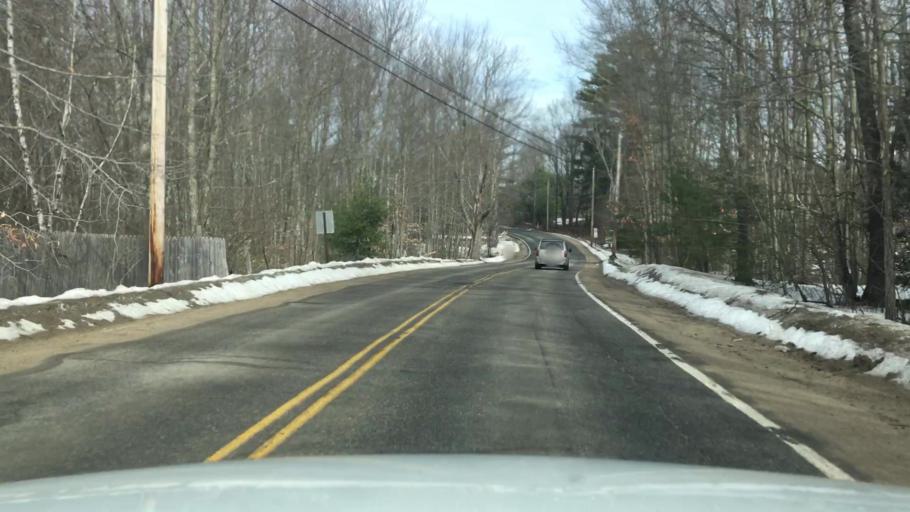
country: US
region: Maine
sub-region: York County
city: Springvale
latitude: 43.4883
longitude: -70.8075
